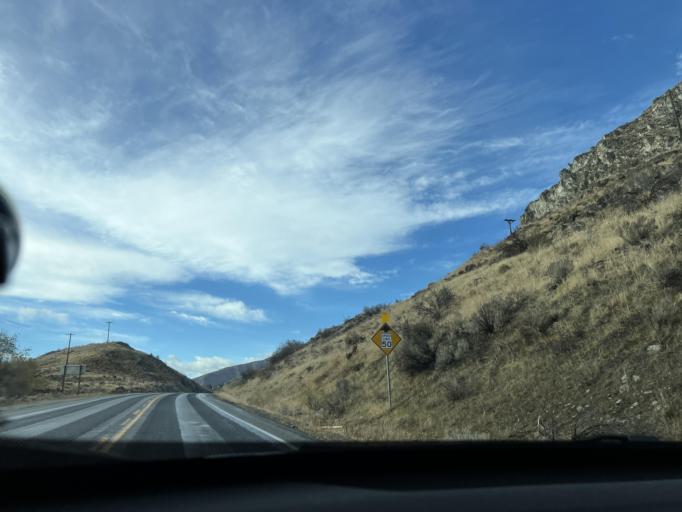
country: US
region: Washington
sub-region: Chelan County
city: Chelan
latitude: 47.8479
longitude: -119.9697
